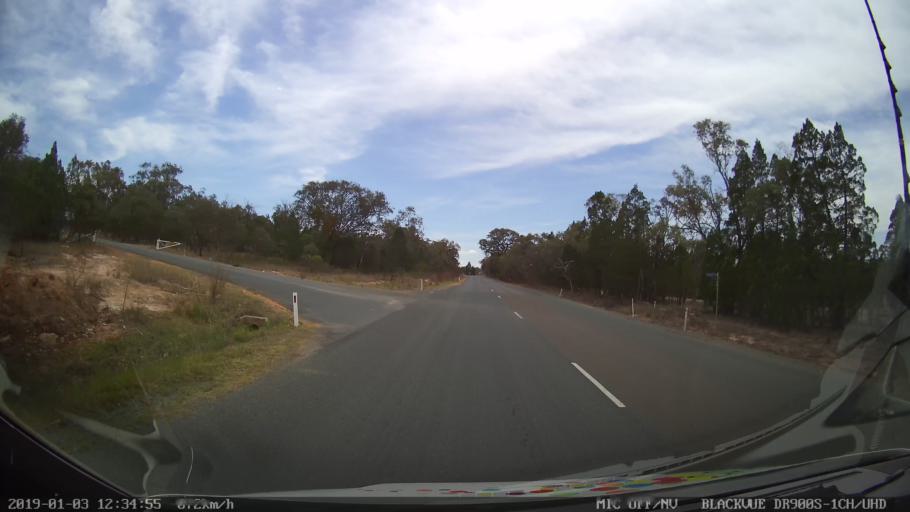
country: AU
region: New South Wales
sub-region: Weddin
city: Grenfell
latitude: -33.8716
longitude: 148.1673
